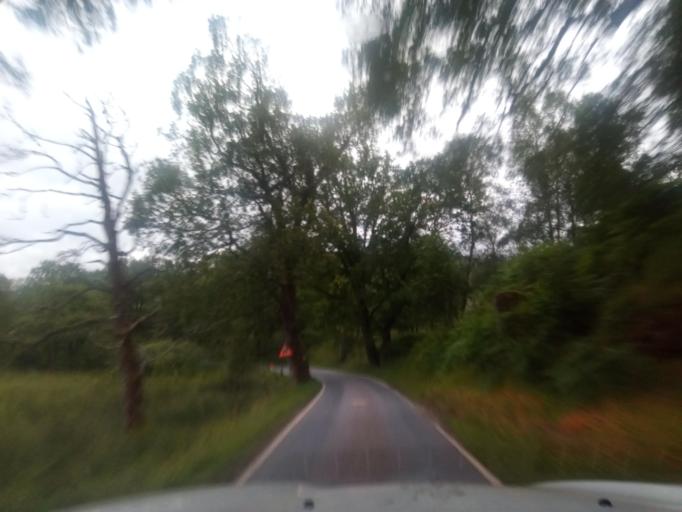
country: GB
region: Scotland
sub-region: Highland
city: Fort William
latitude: 56.8586
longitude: -5.3505
